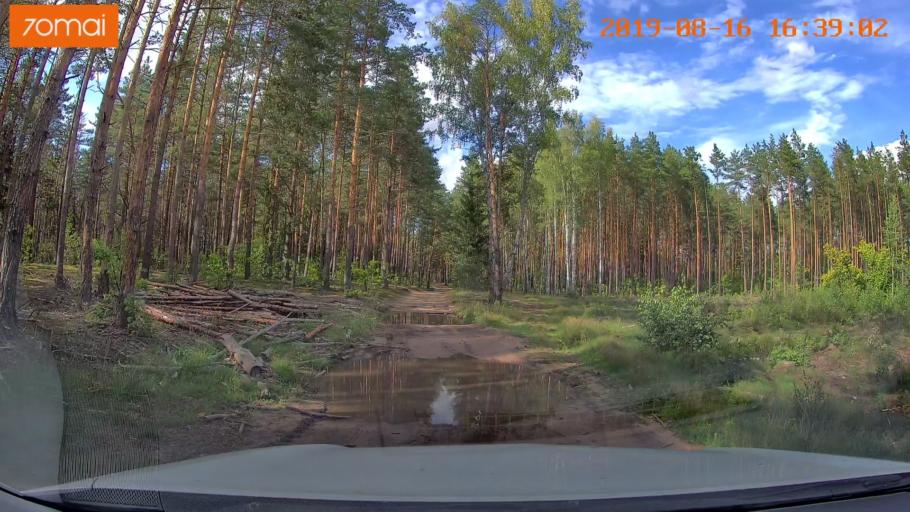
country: BY
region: Mogilev
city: Asipovichy
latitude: 53.2347
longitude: 28.7775
